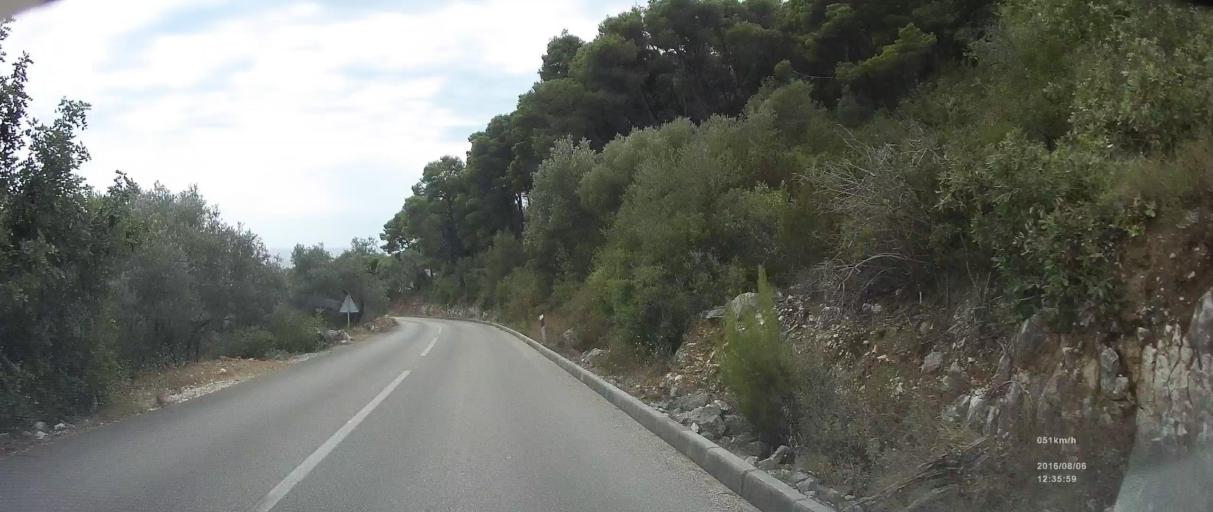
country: HR
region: Dubrovacko-Neretvanska
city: Ston
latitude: 42.7041
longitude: 17.7365
